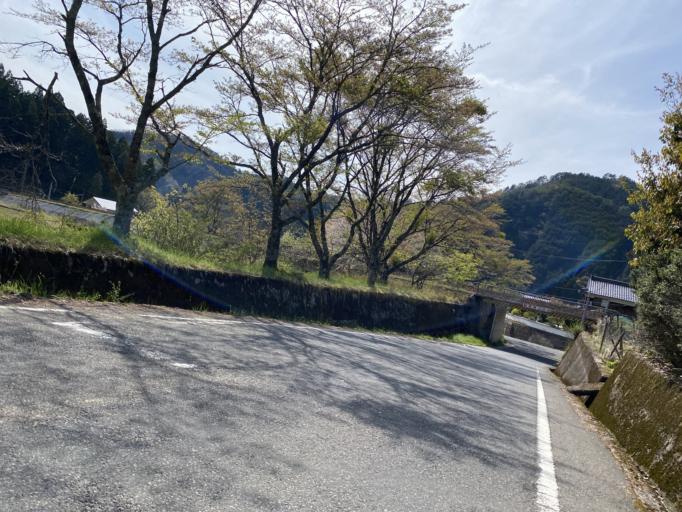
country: JP
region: Hyogo
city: Yamazakicho-nakabirose
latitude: 35.1663
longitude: 134.3381
